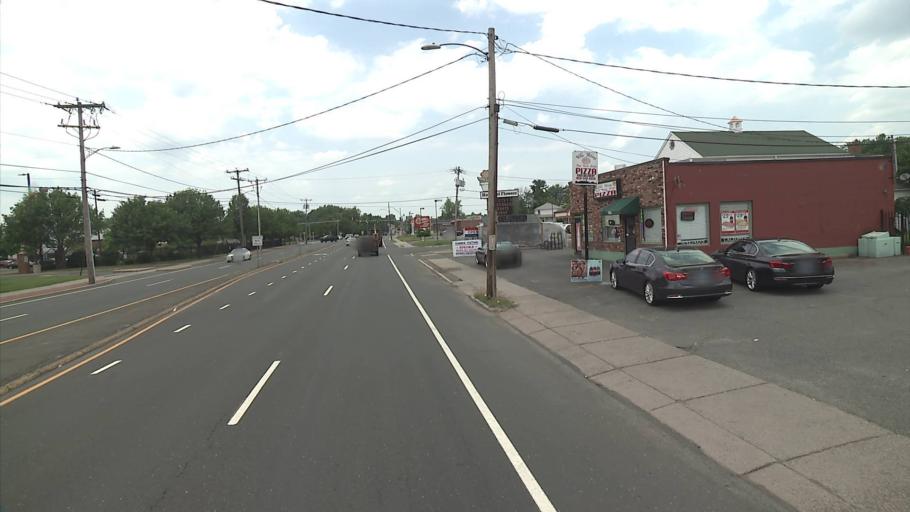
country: US
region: Connecticut
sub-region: Hartford County
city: East Hartford
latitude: 41.7540
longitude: -72.6414
